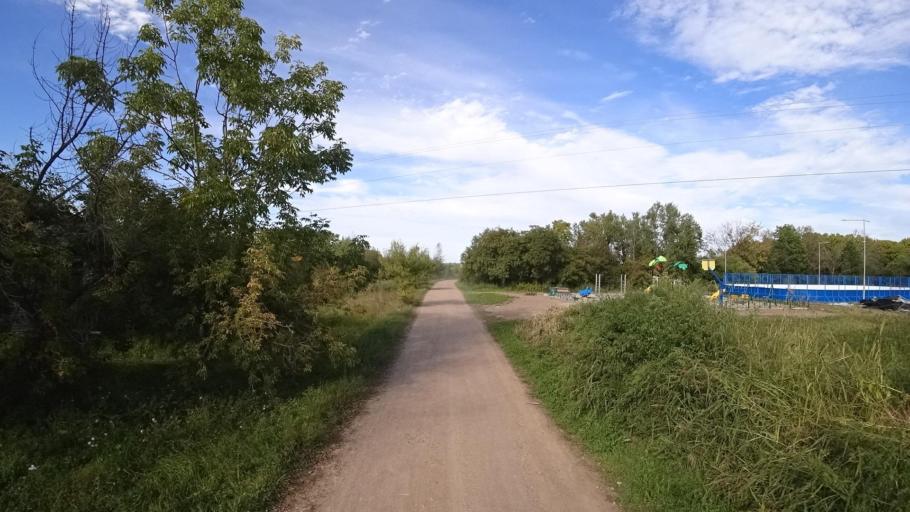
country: RU
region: Primorskiy
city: Dostoyevka
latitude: 44.2992
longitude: 133.4554
